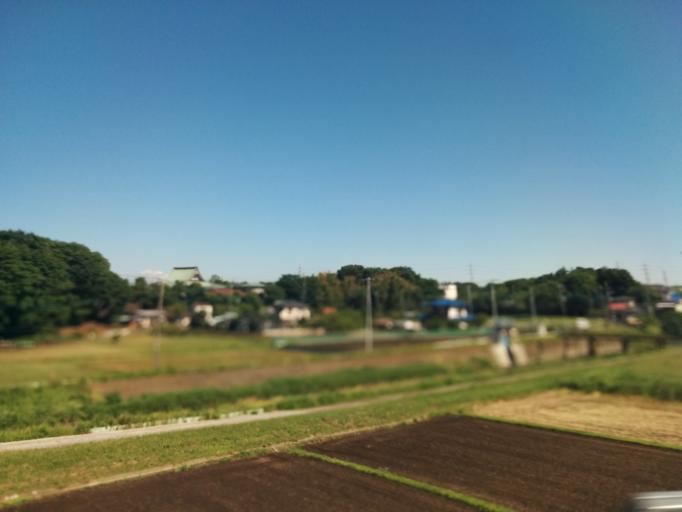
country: JP
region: Kanagawa
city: Atsugi
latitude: 35.4058
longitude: 139.4064
